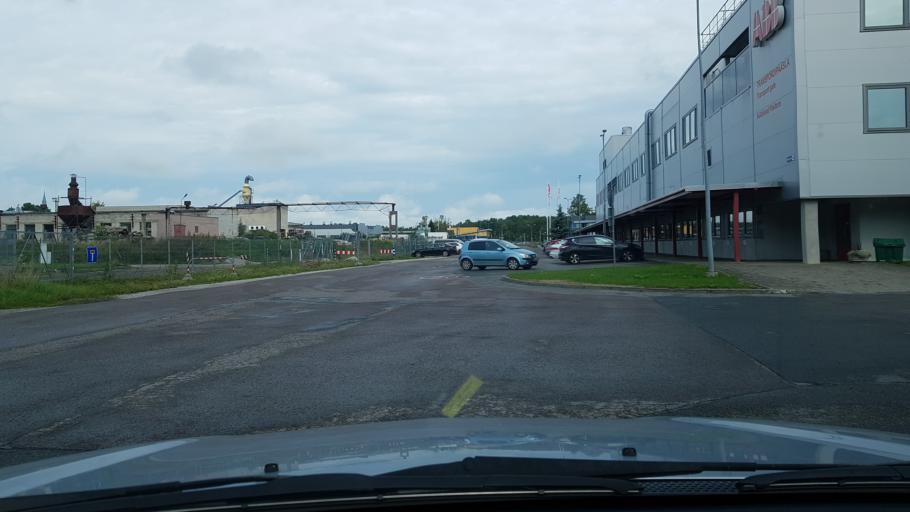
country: EE
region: Harju
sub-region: Rae vald
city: Jueri
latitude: 59.3560
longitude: 24.9291
